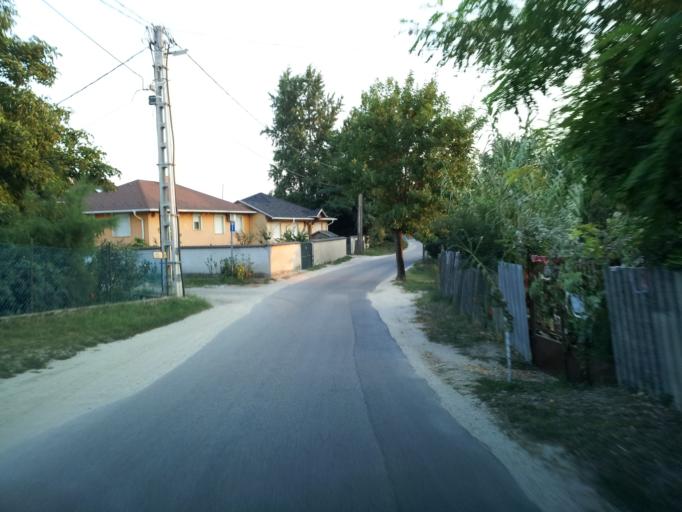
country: HU
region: Pest
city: Szigetszentmiklos
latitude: 47.3263
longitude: 19.0309
